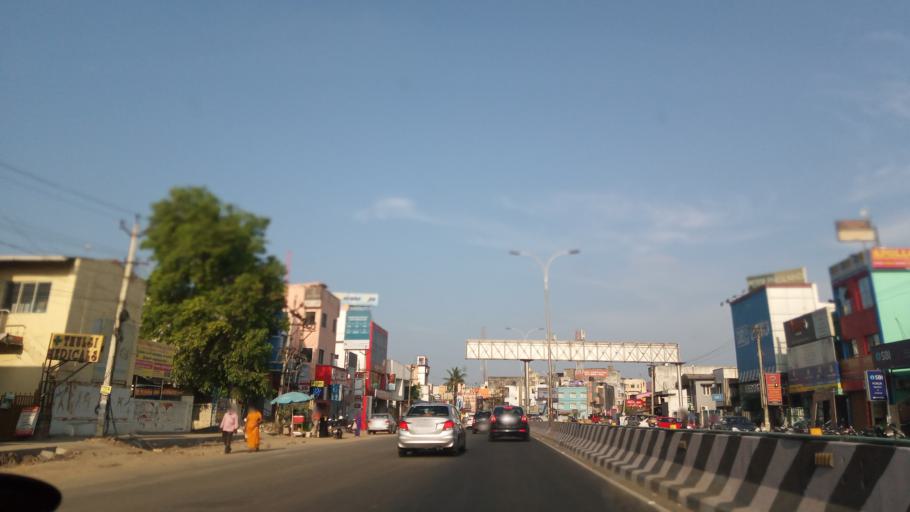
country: IN
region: Tamil Nadu
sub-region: Thiruvallur
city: Porur
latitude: 13.0344
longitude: 80.1585
